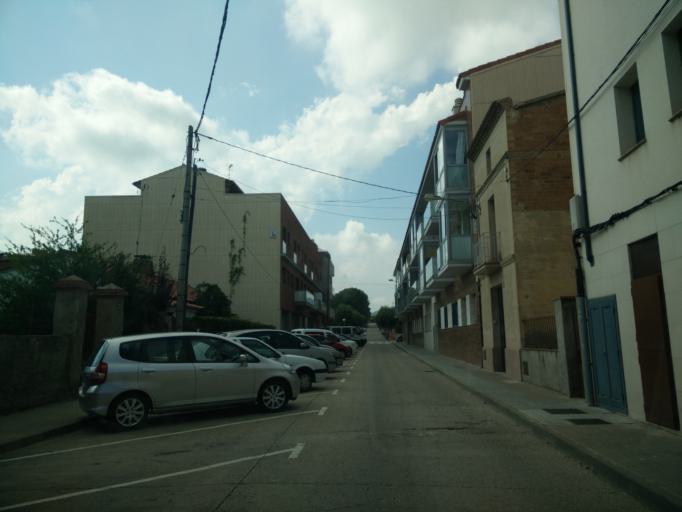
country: ES
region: Catalonia
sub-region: Provincia de Barcelona
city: Piera
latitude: 41.5355
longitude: 1.7687
